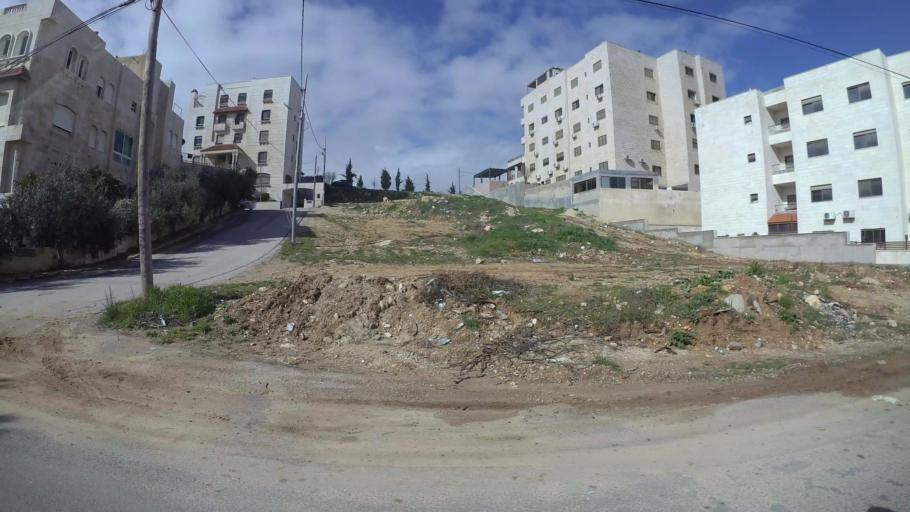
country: JO
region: Amman
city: Al Jubayhah
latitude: 32.0078
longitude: 35.8451
